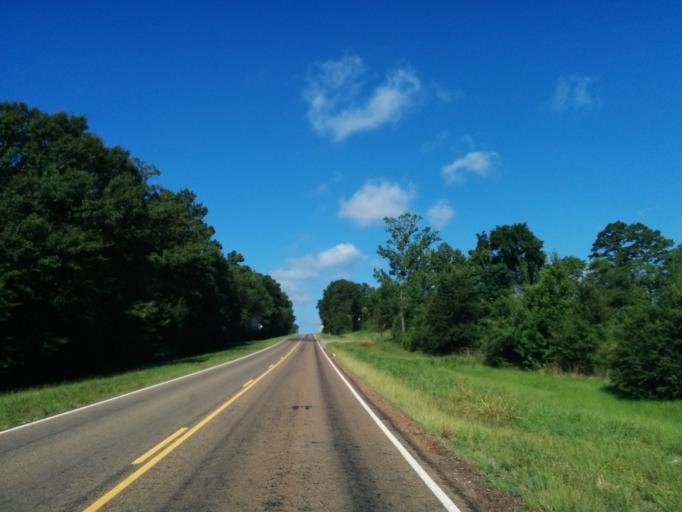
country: US
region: Texas
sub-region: Sabine County
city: Milam
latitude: 31.4291
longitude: -93.9451
